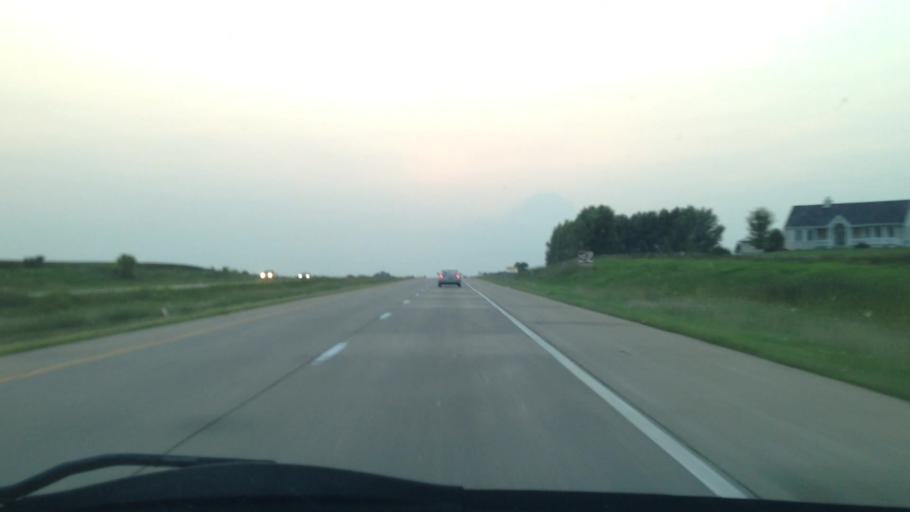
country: US
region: Iowa
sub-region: Buchanan County
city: Jesup
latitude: 42.3324
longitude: -92.0069
